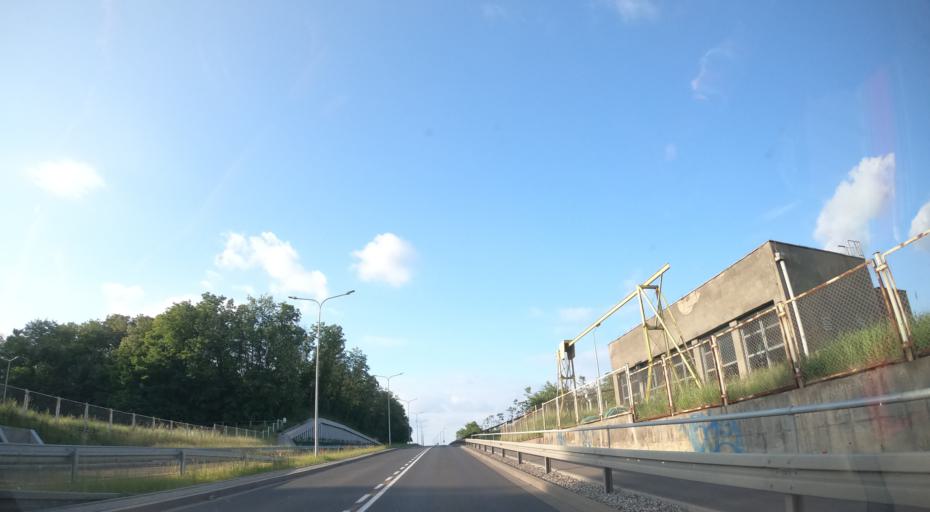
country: PL
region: Lubusz
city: Gorzow Wielkopolski
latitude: 52.7505
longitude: 15.2777
